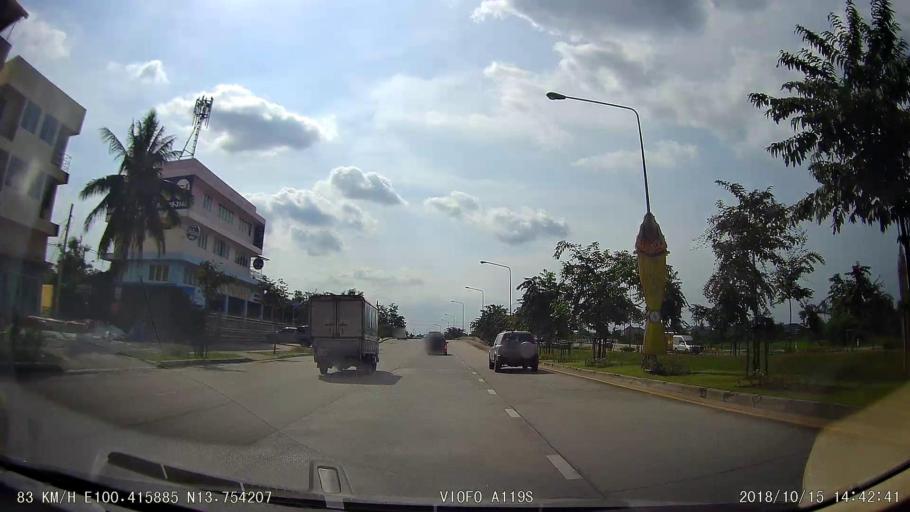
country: TH
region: Bangkok
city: Phasi Charoen
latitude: 13.7542
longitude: 100.4156
